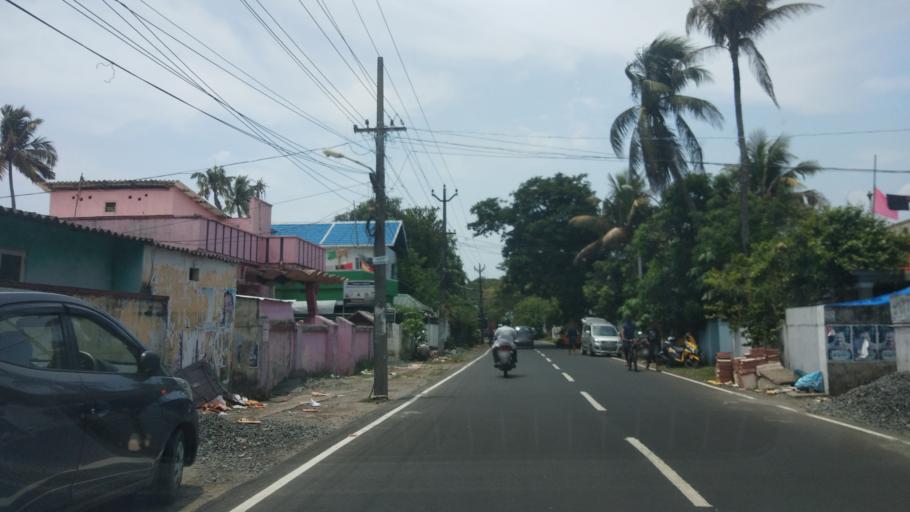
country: IN
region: Kerala
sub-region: Ernakulam
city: Cochin
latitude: 9.9278
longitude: 76.2483
